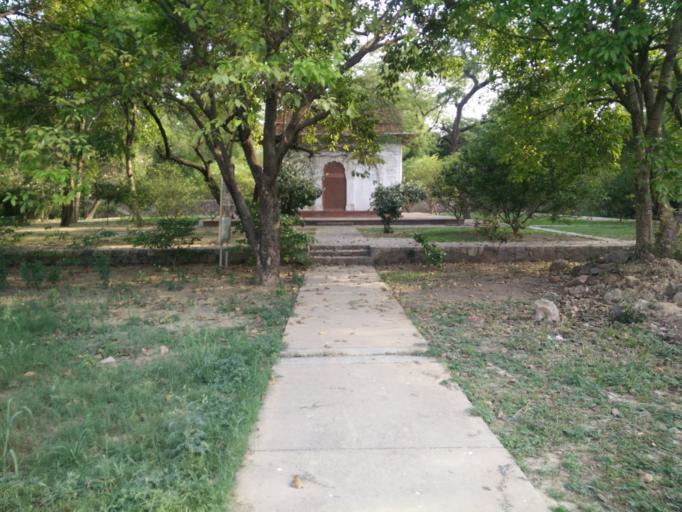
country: IN
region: NCT
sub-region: New Delhi
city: New Delhi
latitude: 28.5977
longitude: 77.2477
